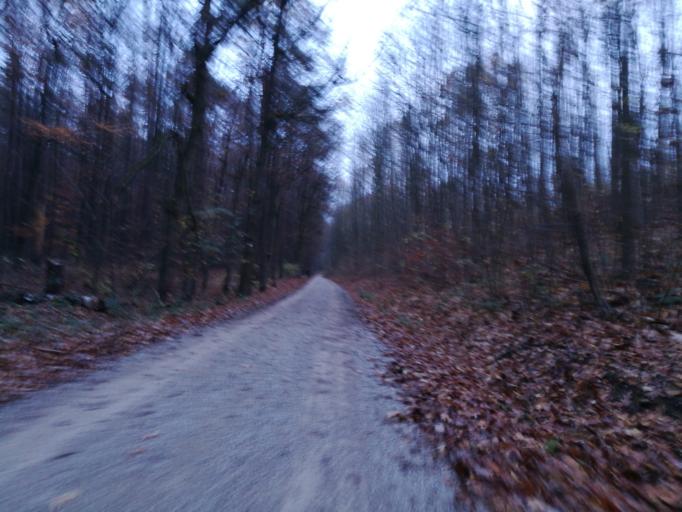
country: DE
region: Bavaria
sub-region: Regierungsbezirk Mittelfranken
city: Seukendorf
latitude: 49.4771
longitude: 10.9205
